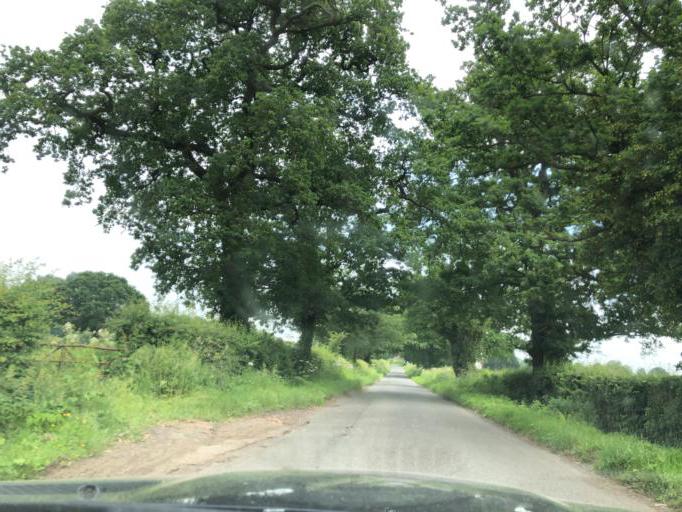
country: GB
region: England
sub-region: Warwickshire
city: Royal Leamington Spa
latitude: 52.3168
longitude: -1.5637
